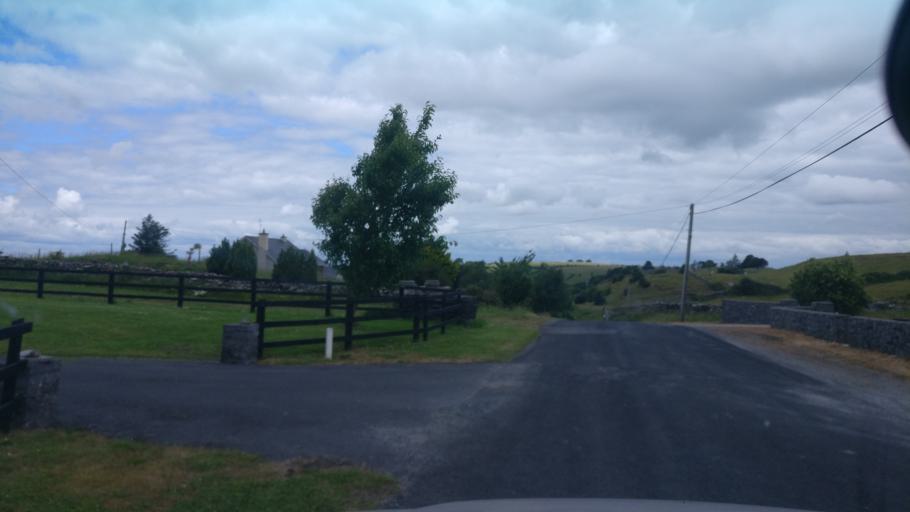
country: IE
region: Connaught
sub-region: County Galway
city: Loughrea
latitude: 53.1747
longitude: -8.5556
